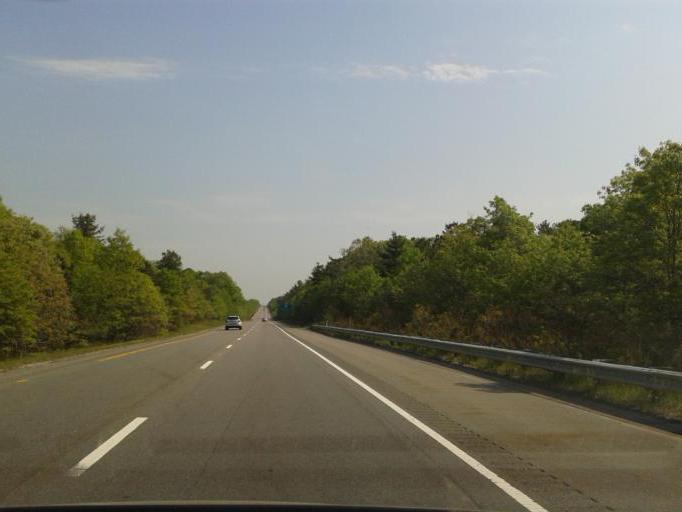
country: US
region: Massachusetts
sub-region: Barnstable County
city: North Falmouth
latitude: 41.6263
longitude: -70.6144
